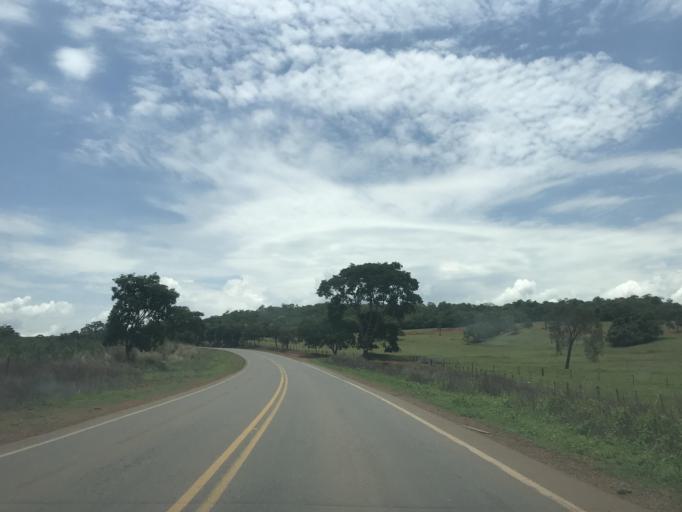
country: BR
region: Goias
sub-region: Vianopolis
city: Vianopolis
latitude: -16.7134
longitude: -48.4033
